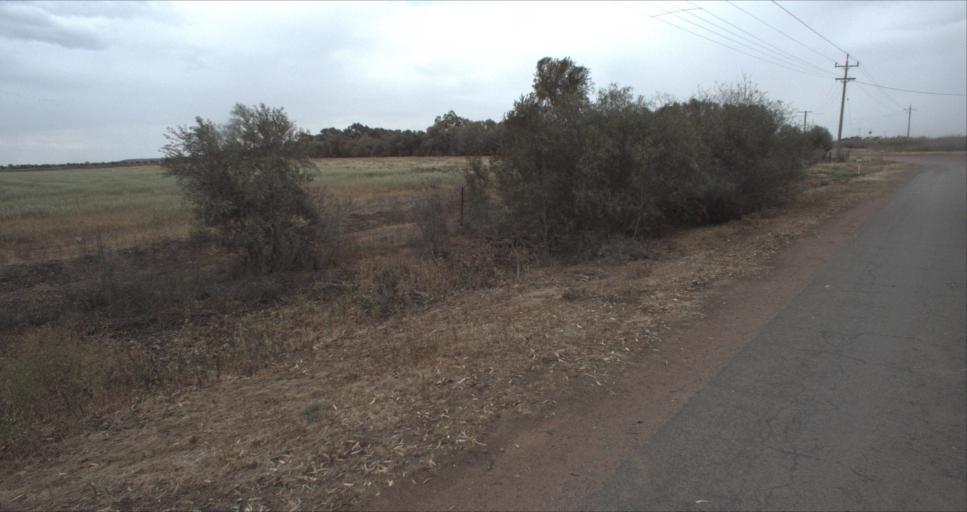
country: AU
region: New South Wales
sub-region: Leeton
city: Leeton
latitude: -34.4047
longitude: 146.3415
